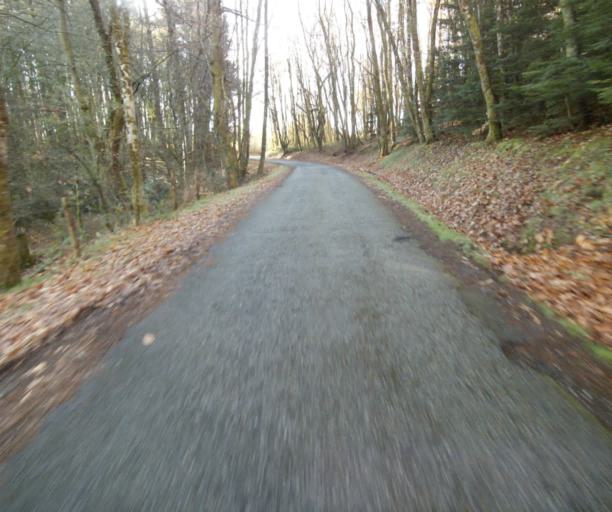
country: FR
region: Limousin
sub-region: Departement de la Correze
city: Laguenne
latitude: 45.2770
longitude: 1.8620
